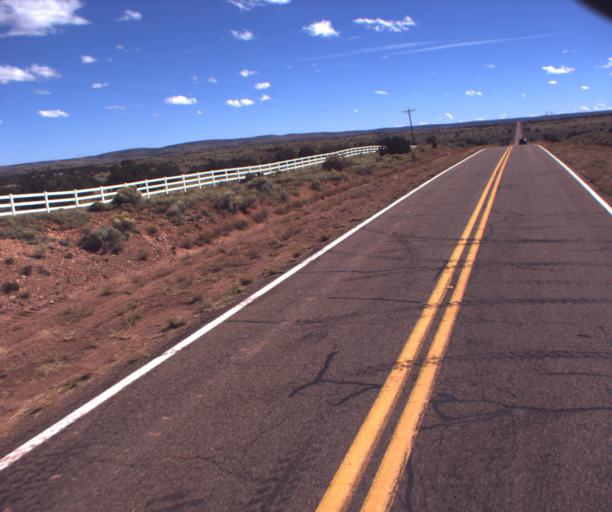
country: US
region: Arizona
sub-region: Apache County
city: Saint Johns
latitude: 34.5825
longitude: -109.6416
